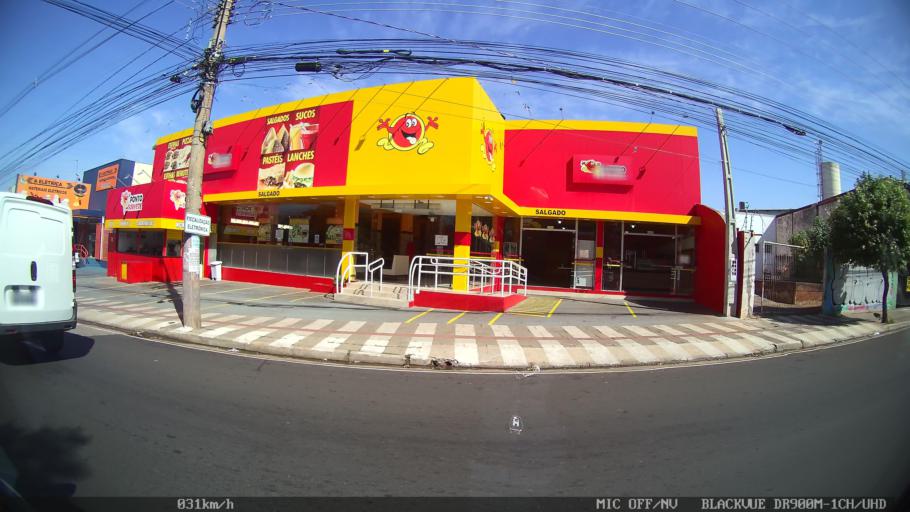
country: BR
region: Sao Paulo
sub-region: Sao Jose Do Rio Preto
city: Sao Jose do Rio Preto
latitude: -20.7783
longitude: -49.4036
